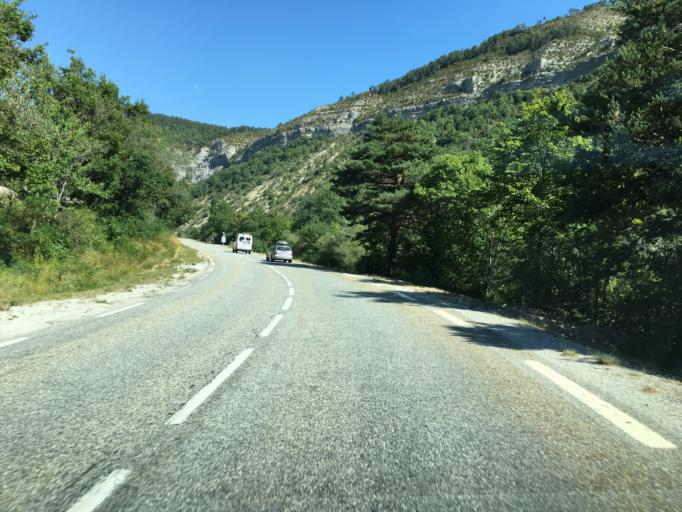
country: FR
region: Provence-Alpes-Cote d'Azur
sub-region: Departement des Hautes-Alpes
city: Veynes
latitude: 44.5463
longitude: 5.7786
